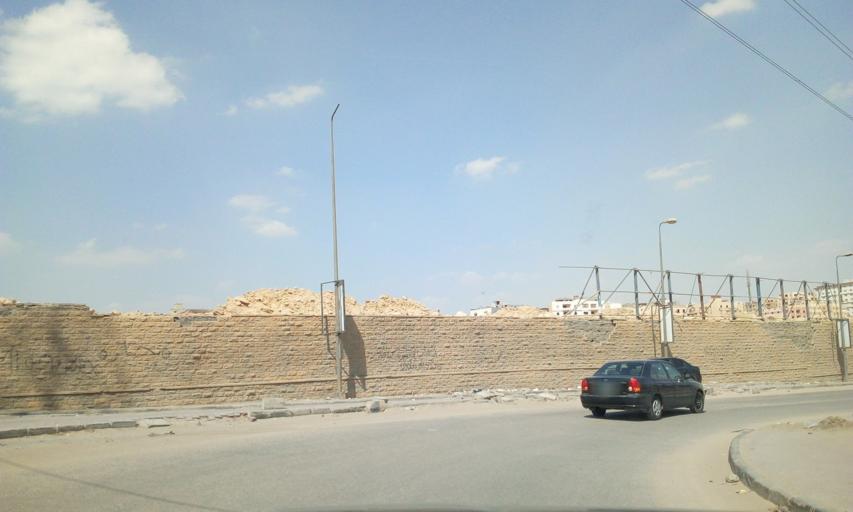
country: EG
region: Muhafazat al Qahirah
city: Cairo
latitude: 29.9846
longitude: 31.3166
